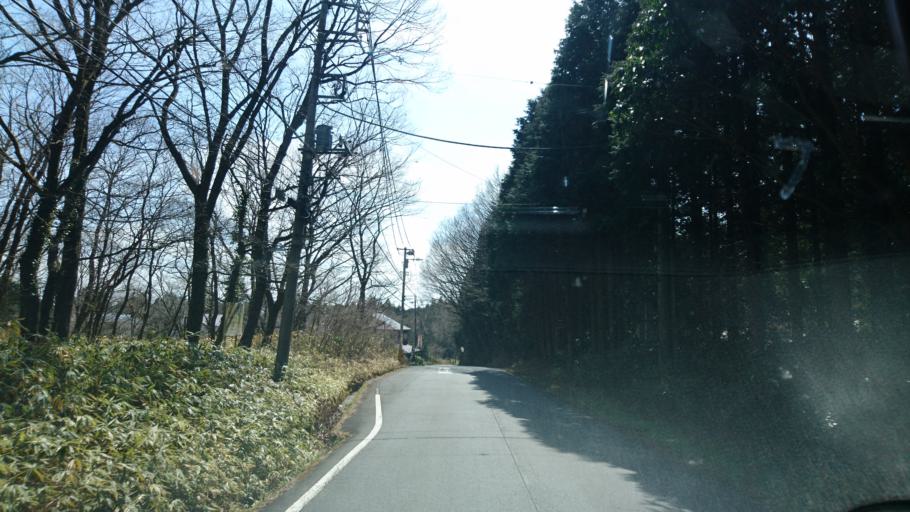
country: JP
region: Shizuoka
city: Fujinomiya
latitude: 35.3400
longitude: 138.5740
